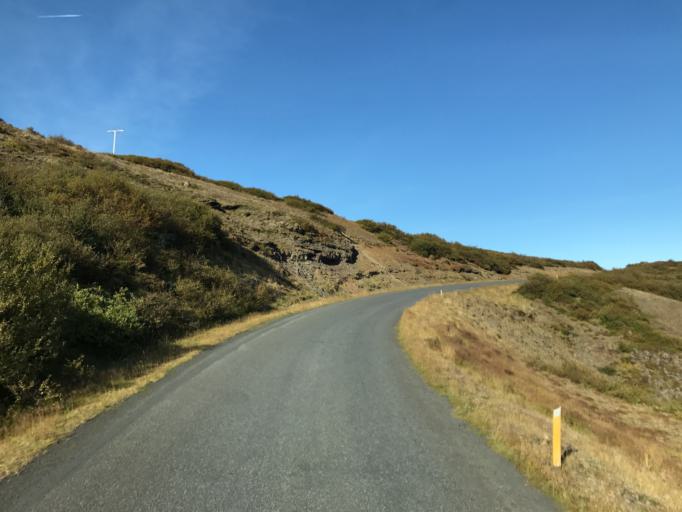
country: IS
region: South
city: Hveragerdi
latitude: 64.1563
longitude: -21.2529
